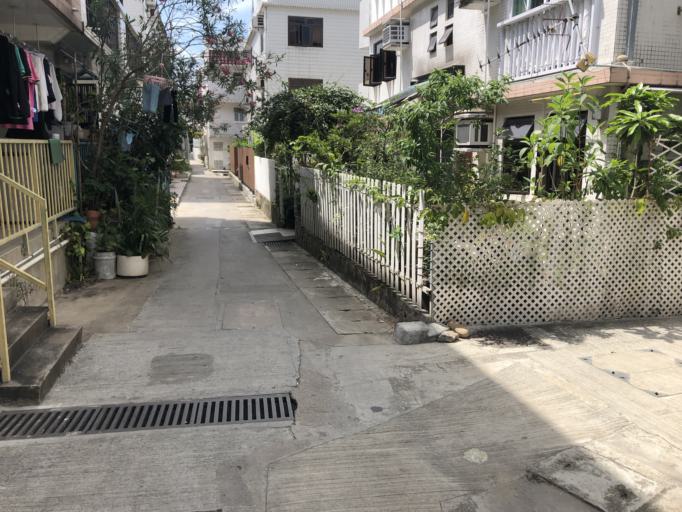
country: HK
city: Yung Shue Wan
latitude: 22.2238
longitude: 114.1124
